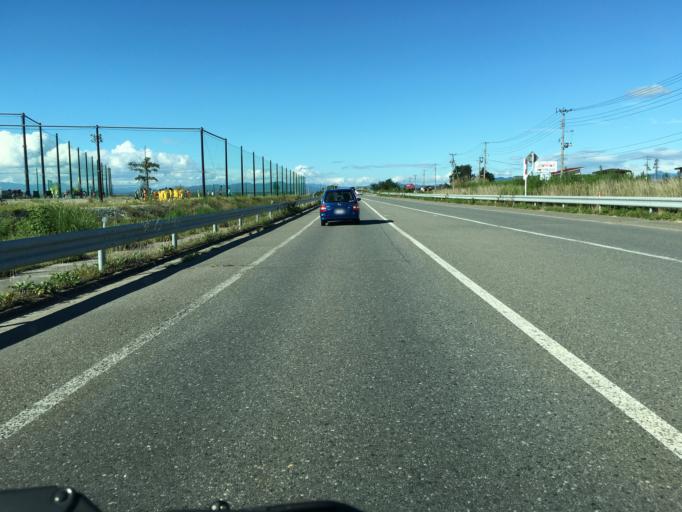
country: JP
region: Yamagata
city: Yonezawa
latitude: 37.9279
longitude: 140.1086
